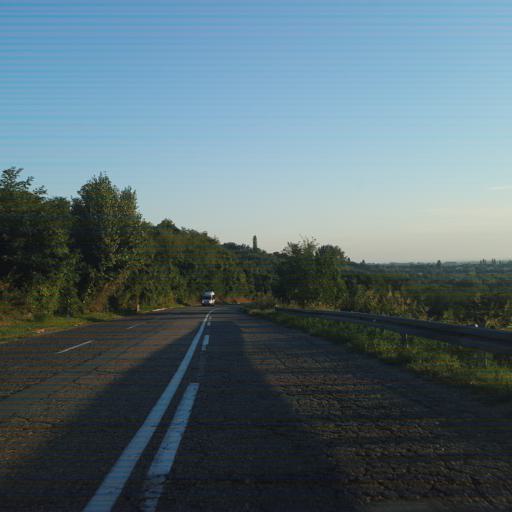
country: RS
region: Central Serbia
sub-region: Borski Okrug
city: Negotin
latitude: 44.2268
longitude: 22.5004
